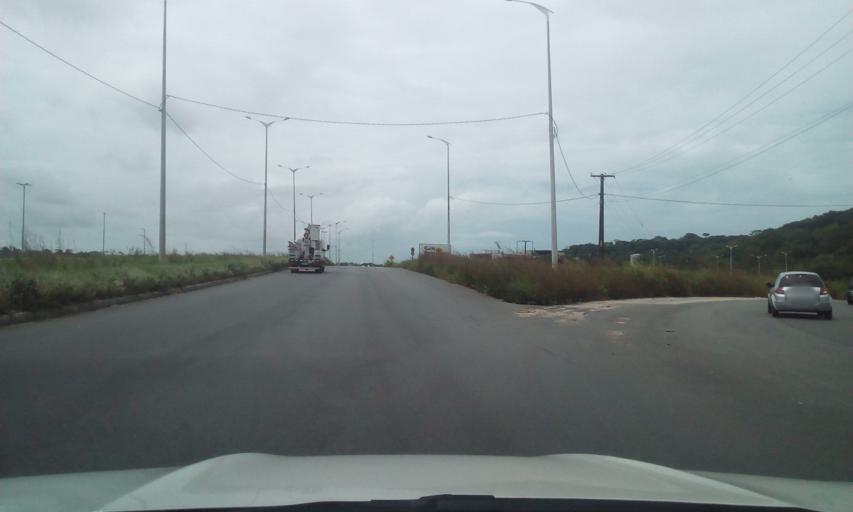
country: BR
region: Pernambuco
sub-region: Abreu E Lima
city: Abreu e Lima
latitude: -7.9226
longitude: -34.8951
